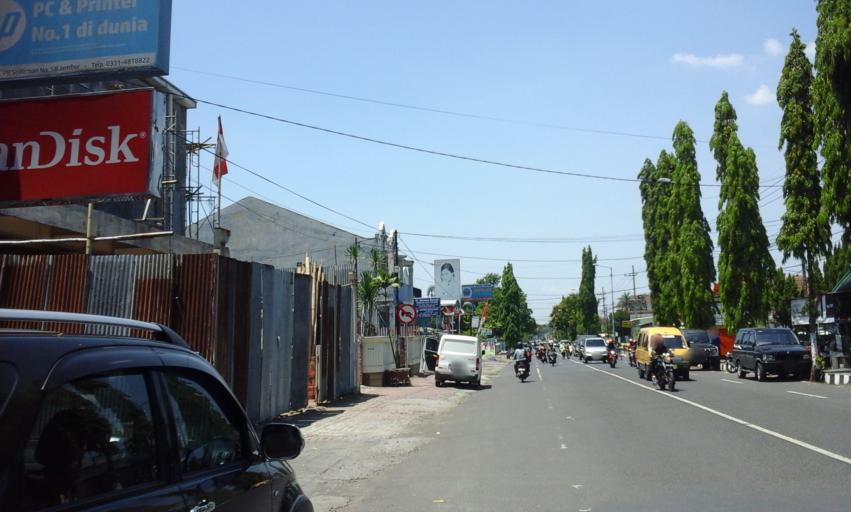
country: ID
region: East Java
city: Krajan
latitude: -8.1633
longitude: 113.7068
